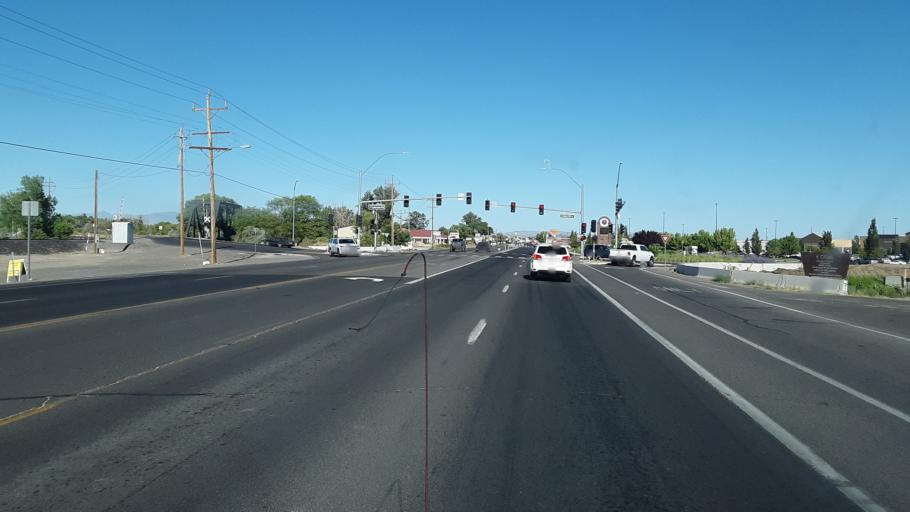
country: US
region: Nevada
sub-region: Churchill County
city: Fallon
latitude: 39.4785
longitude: -118.8095
